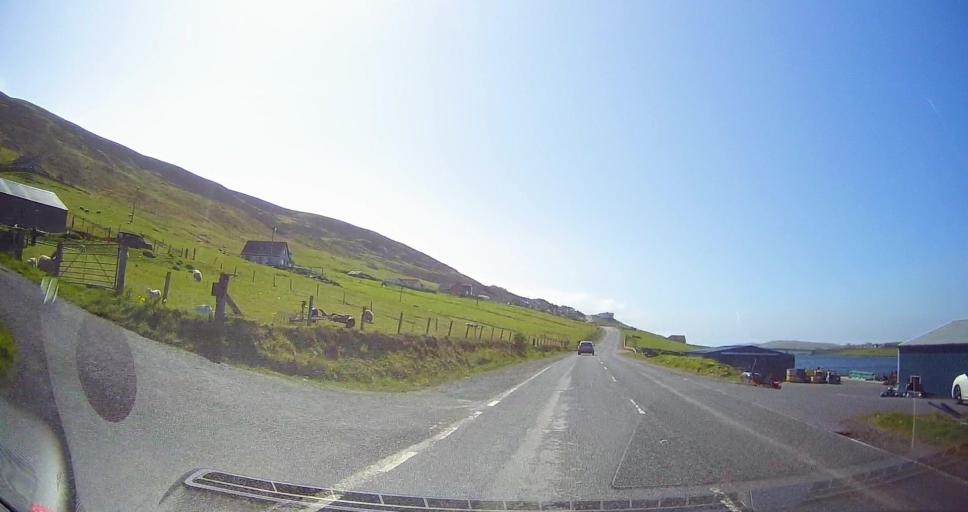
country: GB
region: Scotland
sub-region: Shetland Islands
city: Lerwick
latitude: 60.1365
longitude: -1.2666
